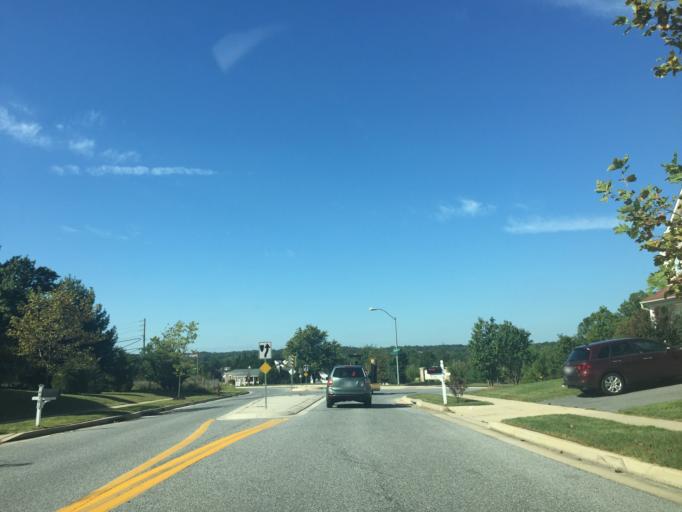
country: US
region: Maryland
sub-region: Baltimore County
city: Rossville
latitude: 39.3713
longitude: -76.4863
